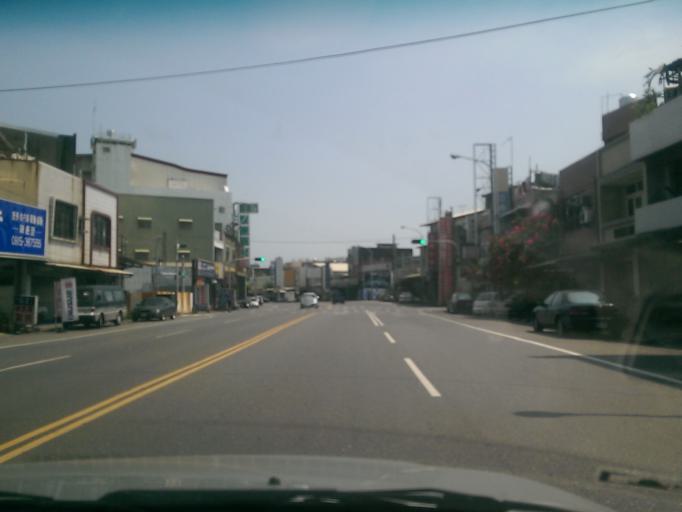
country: TW
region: Taiwan
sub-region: Chiayi
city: Taibao
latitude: 23.5796
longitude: 120.2982
